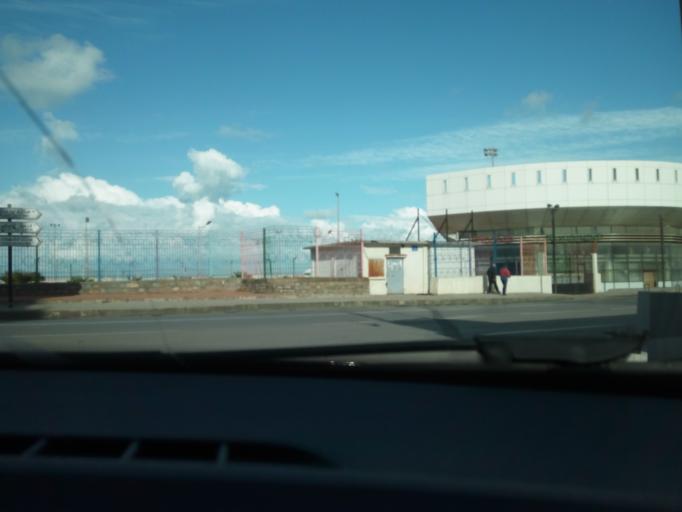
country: DZ
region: Alger
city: Algiers
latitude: 36.7958
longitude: 3.0512
